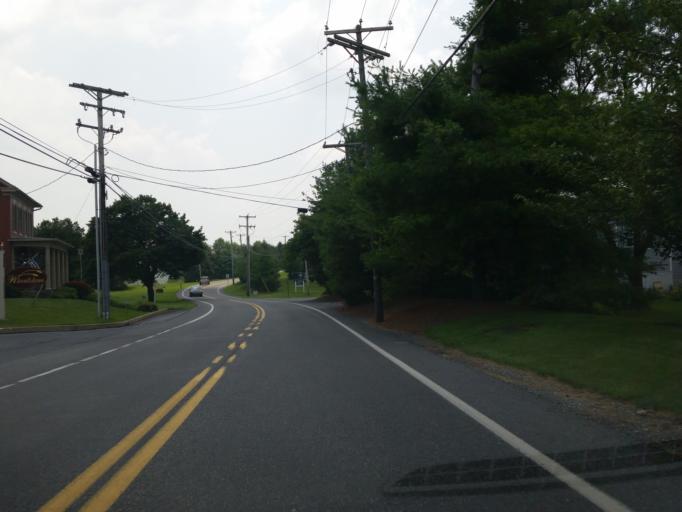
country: US
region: Pennsylvania
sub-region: Dauphin County
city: Palmdale
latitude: 40.2922
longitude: -76.6012
